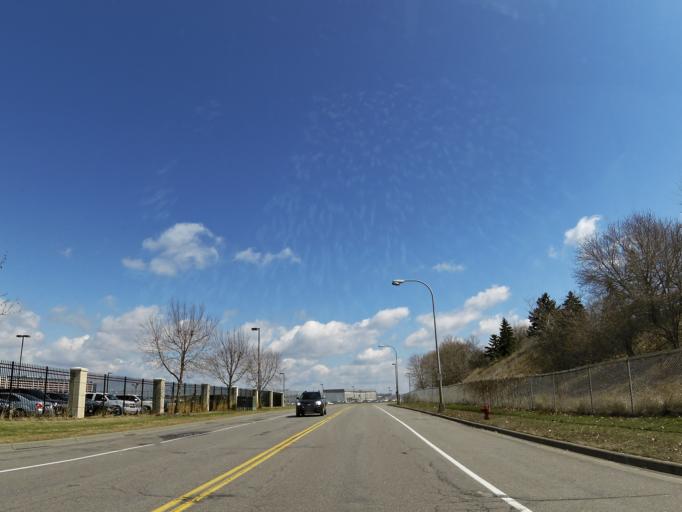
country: US
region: Minnesota
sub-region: Hennepin County
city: Richfield
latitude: 44.8765
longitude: -93.2165
